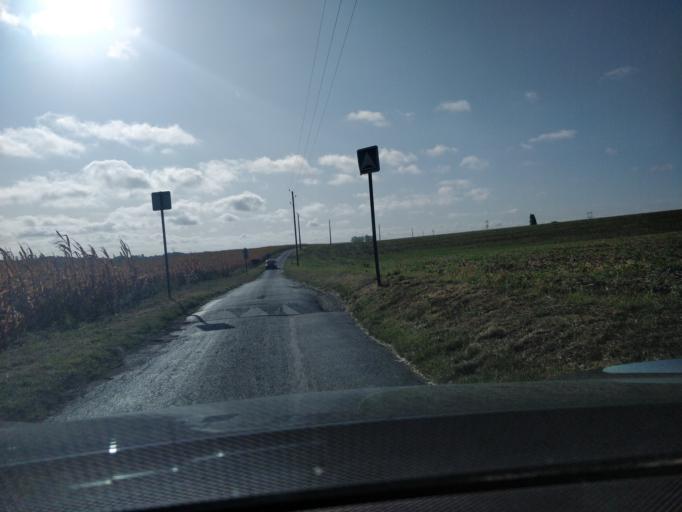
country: FR
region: Ile-de-France
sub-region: Departement de l'Essonne
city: Forges-les-Bains
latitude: 48.6229
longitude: 2.1034
